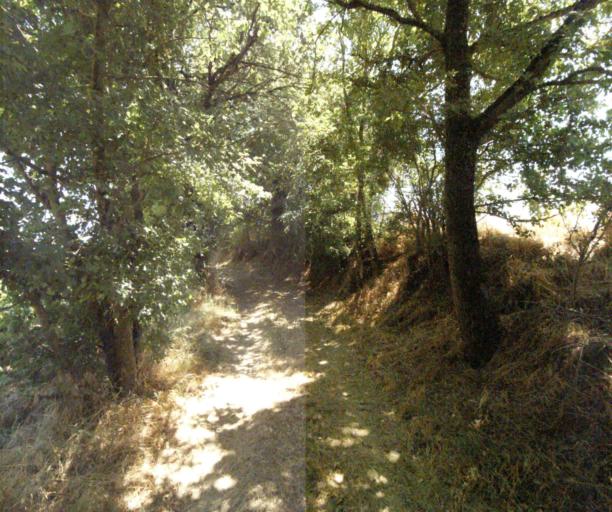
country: FR
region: Midi-Pyrenees
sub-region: Departement de la Haute-Garonne
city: Saint-Felix-Lauragais
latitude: 43.4789
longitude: 1.8483
